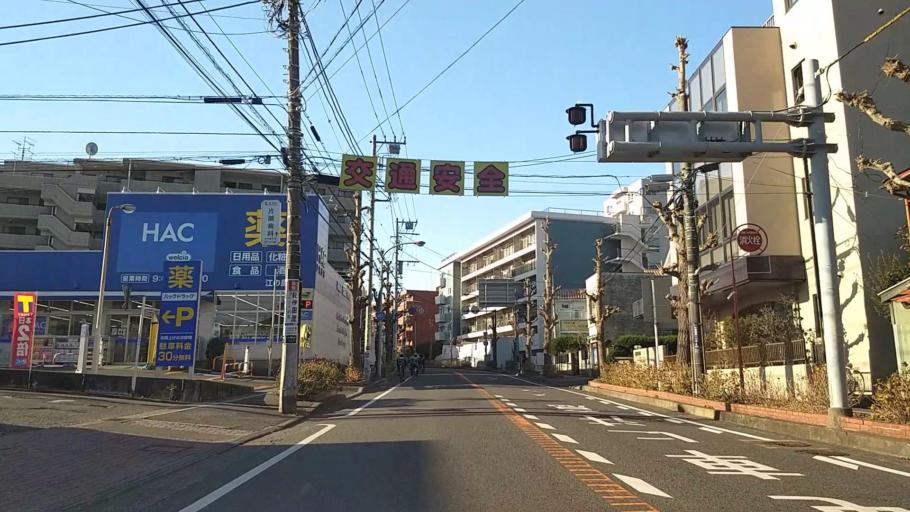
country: JP
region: Kanagawa
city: Fujisawa
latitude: 35.3106
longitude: 139.4890
